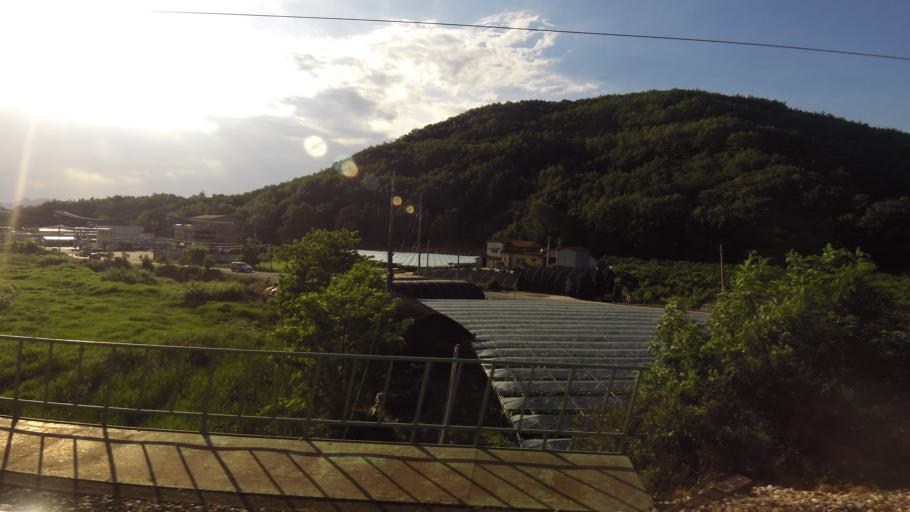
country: KR
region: Chungcheongbuk-do
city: Yong-dong
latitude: 36.1677
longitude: 127.8142
